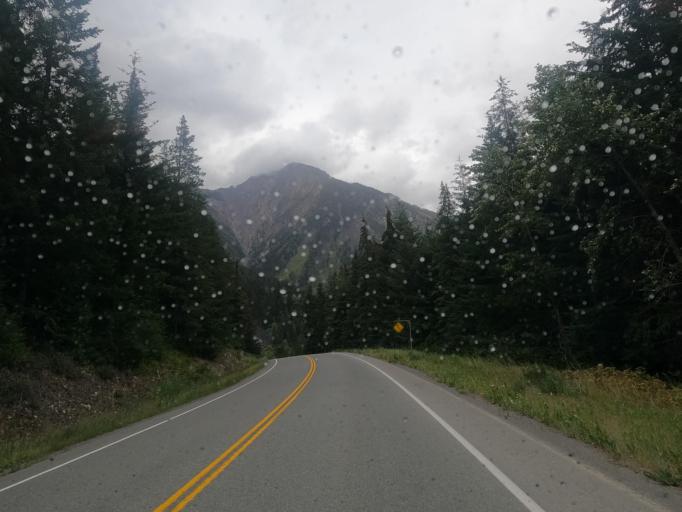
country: CA
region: British Columbia
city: Lillooet
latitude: 50.5252
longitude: -122.1613
